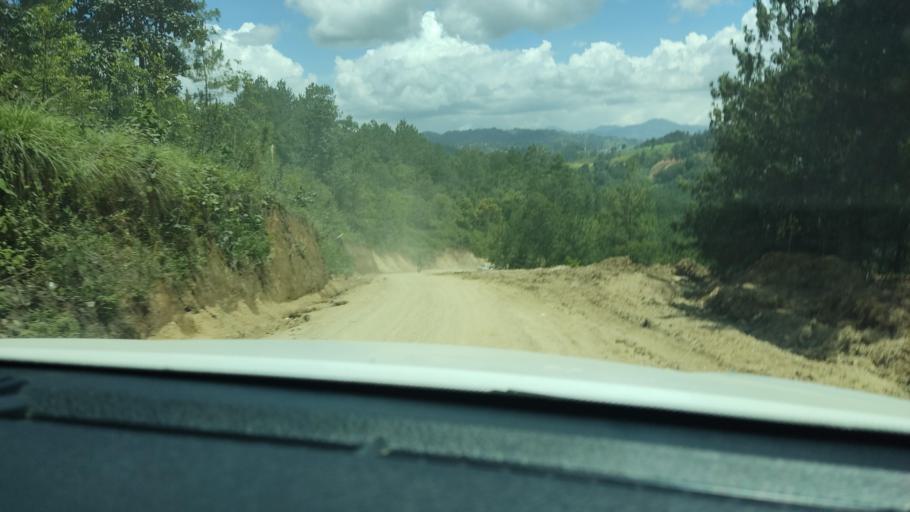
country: GT
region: Chimaltenango
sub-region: Municipio de San Juan Comalapa
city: Comalapa
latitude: 14.7674
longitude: -90.8814
